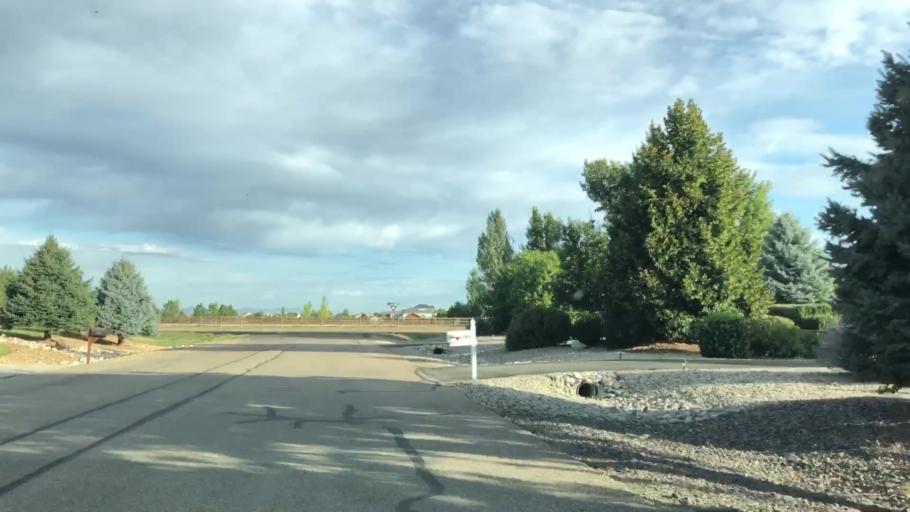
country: US
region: Colorado
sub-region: Weld County
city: Windsor
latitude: 40.4433
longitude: -104.9534
